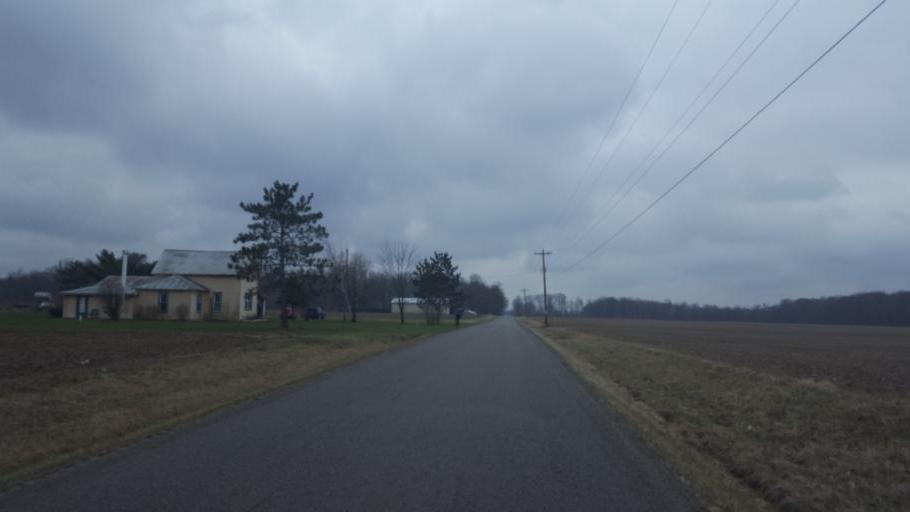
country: US
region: Ohio
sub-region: Delaware County
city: Ashley
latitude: 40.3719
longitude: -82.8542
